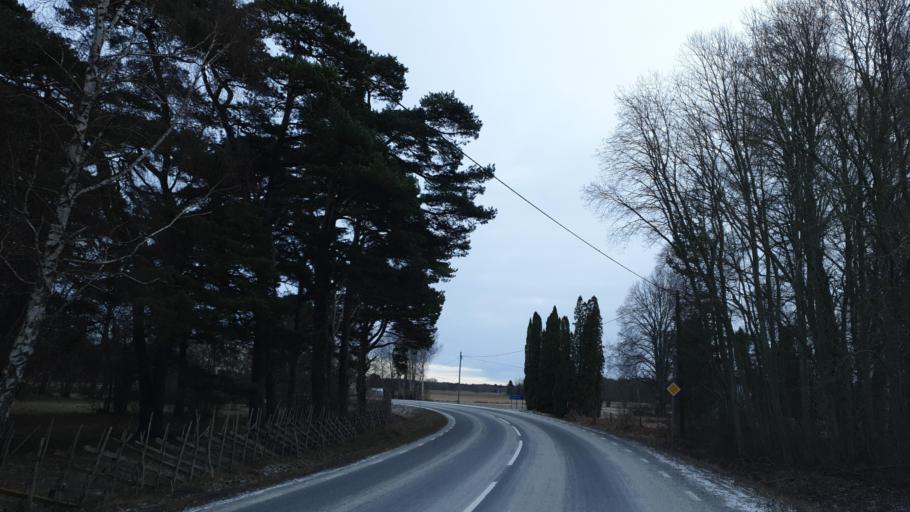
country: SE
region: Gotland
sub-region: Gotland
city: Slite
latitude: 57.4203
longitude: 18.8610
